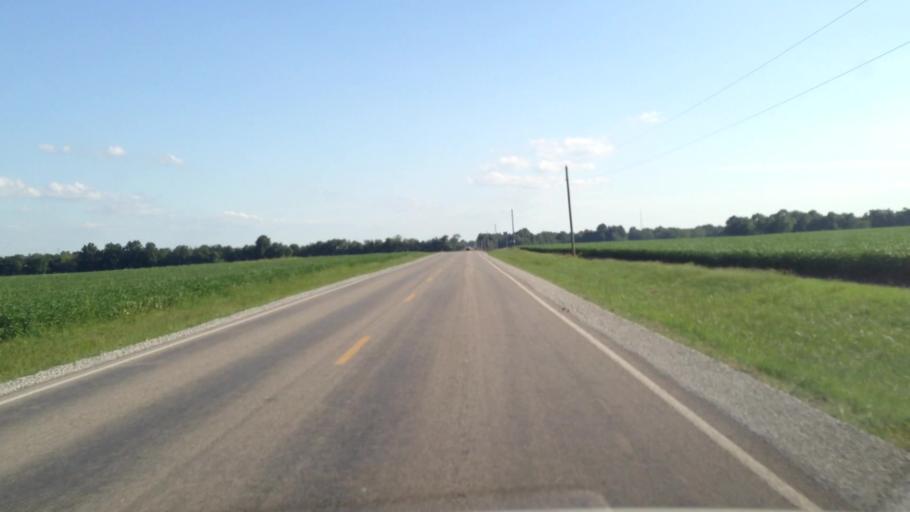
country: US
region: Kansas
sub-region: Crawford County
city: Pittsburg
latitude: 37.3591
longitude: -94.6315
